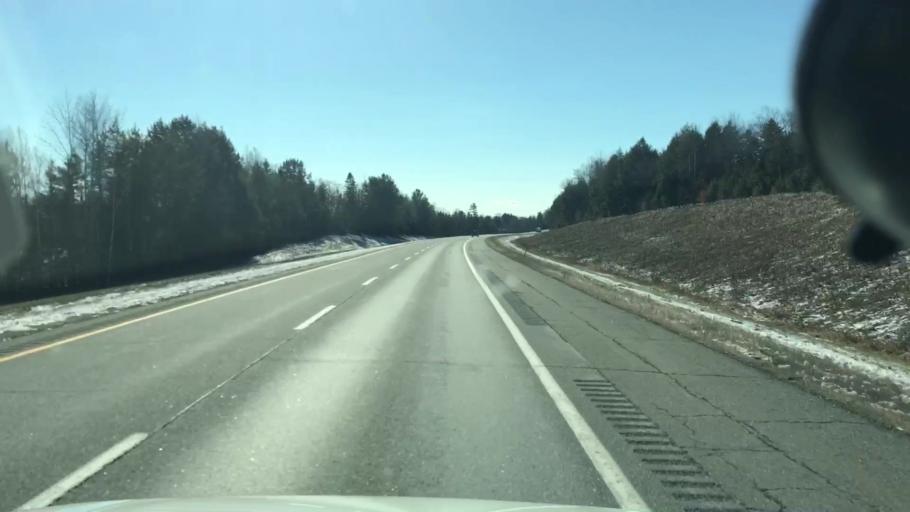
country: US
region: Maine
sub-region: Penobscot County
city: Howland
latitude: 45.2915
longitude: -68.6655
